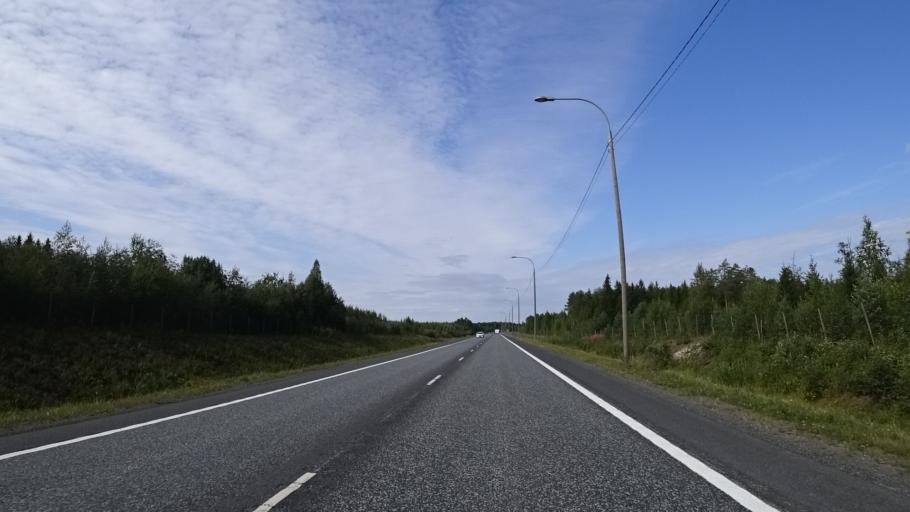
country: FI
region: North Karelia
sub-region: Joensuu
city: Pyhaeselkae
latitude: 62.5254
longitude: 29.8728
